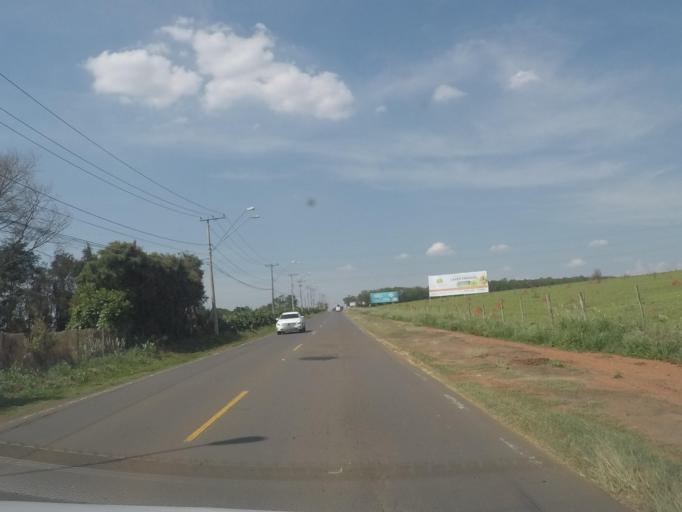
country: BR
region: Sao Paulo
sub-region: Sumare
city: Sumare
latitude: -22.8491
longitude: -47.2831
